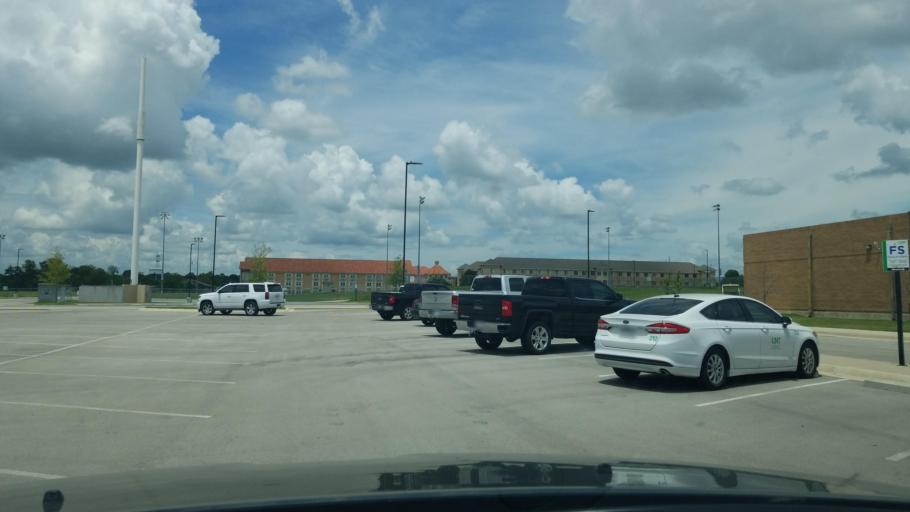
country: US
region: Texas
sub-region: Denton County
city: Denton
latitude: 33.2080
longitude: -97.1570
